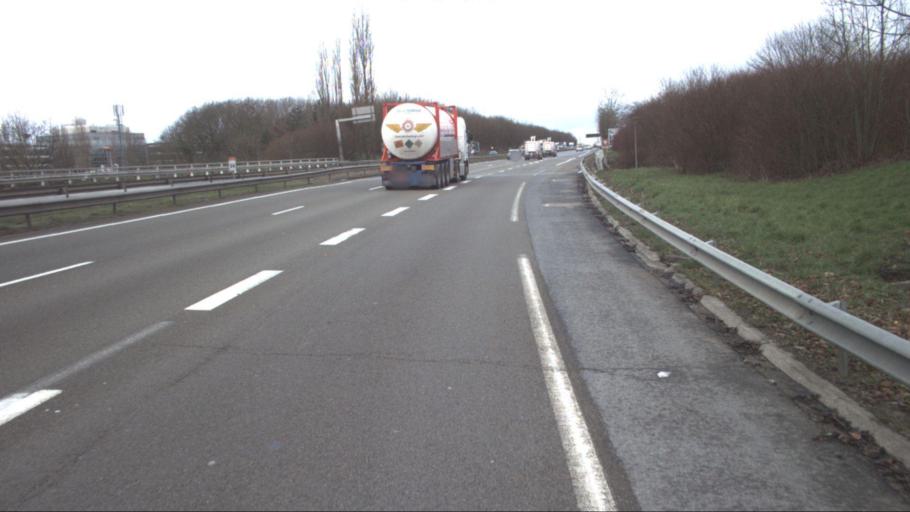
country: FR
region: Ile-de-France
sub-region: Departement des Yvelines
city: Saint-Cyr-l'Ecole
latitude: 48.7886
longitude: 2.0618
